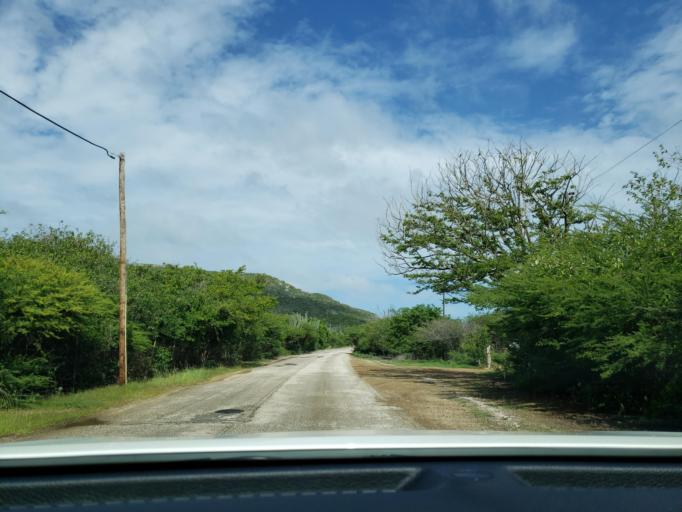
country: CW
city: Barber
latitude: 12.3120
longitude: -69.0908
